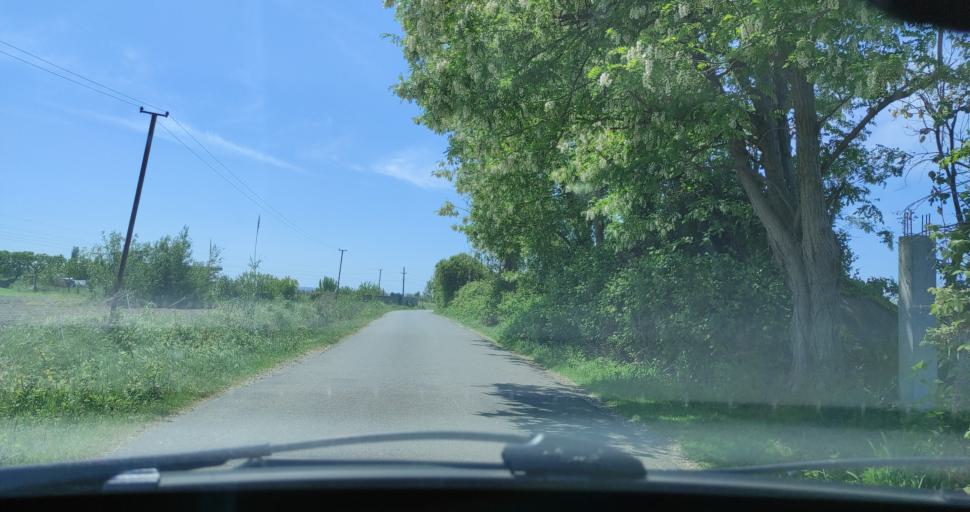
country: AL
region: Lezhe
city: Lezhe
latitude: 41.7562
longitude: 19.6114
